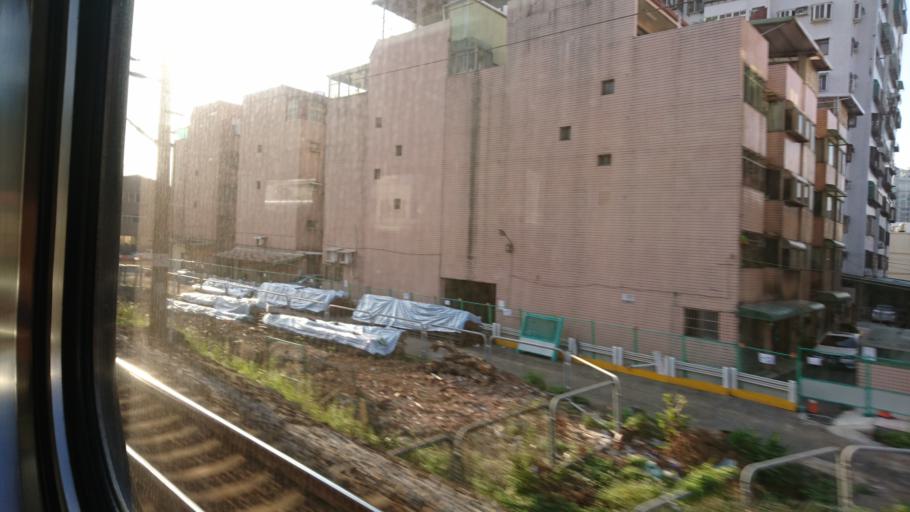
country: TW
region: Taiwan
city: Daxi
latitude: 24.9419
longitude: 121.2136
